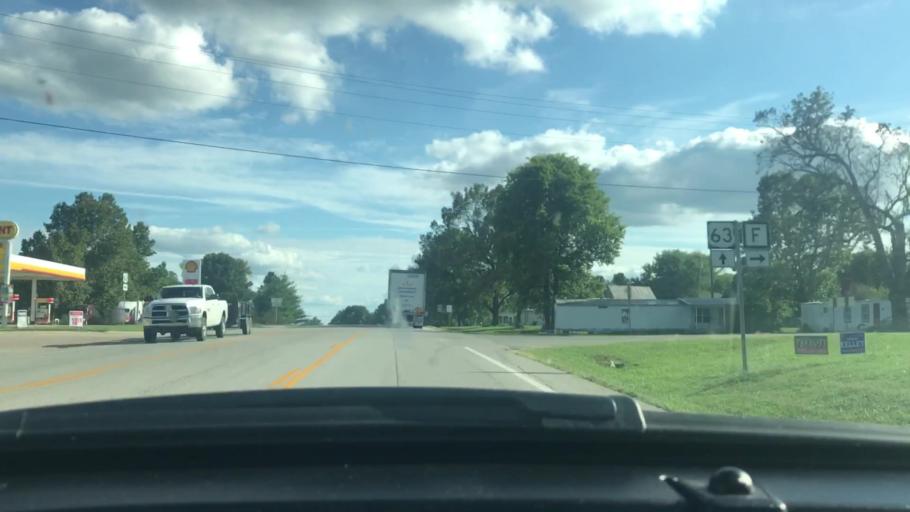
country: US
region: Missouri
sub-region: Oregon County
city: Thayer
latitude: 36.5952
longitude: -91.6440
